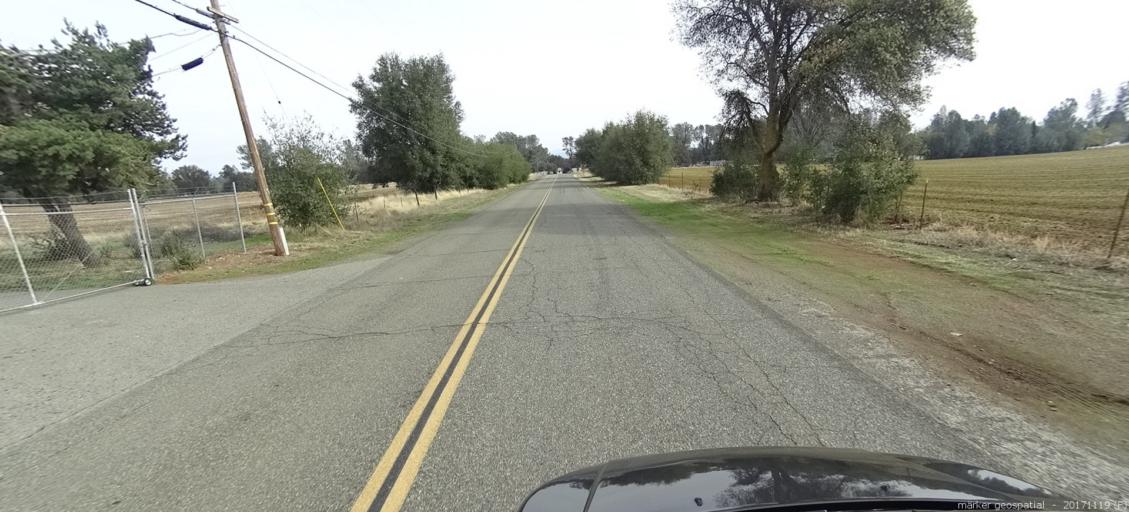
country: US
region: California
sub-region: Shasta County
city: Anderson
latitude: 40.4913
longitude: -122.2769
